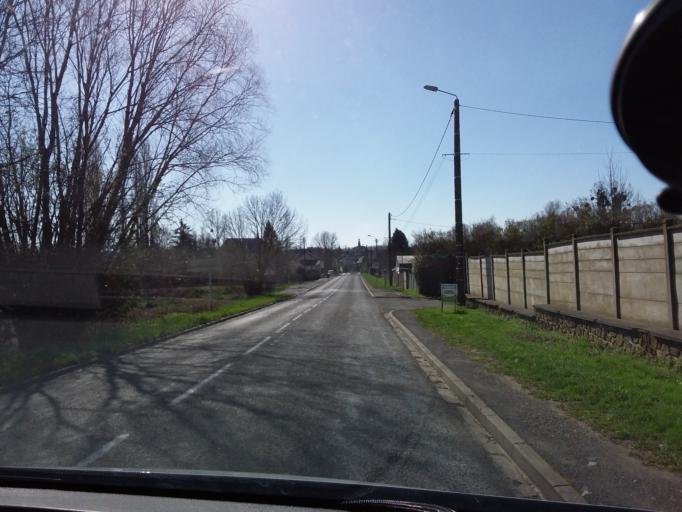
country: FR
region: Picardie
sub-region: Departement de l'Aisne
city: Montcornet
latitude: 49.7002
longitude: 4.0147
